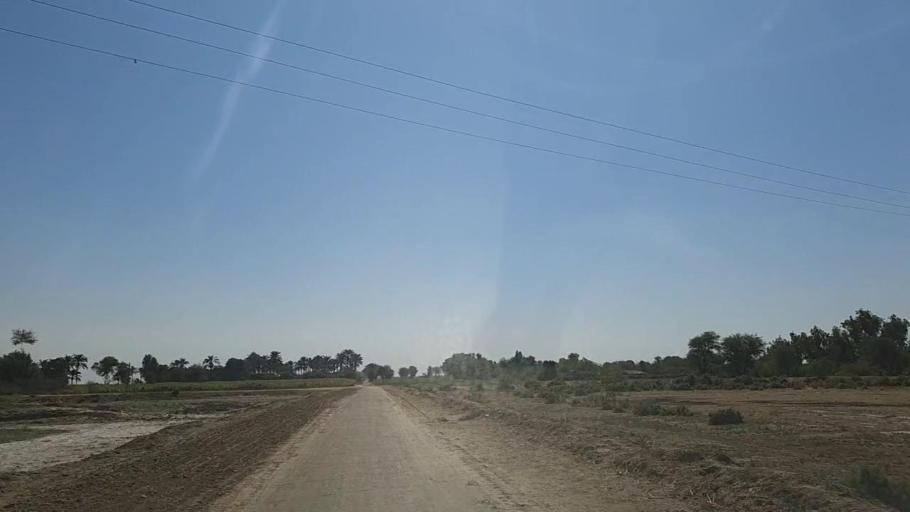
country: PK
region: Sindh
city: Samaro
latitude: 25.2936
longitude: 69.5027
